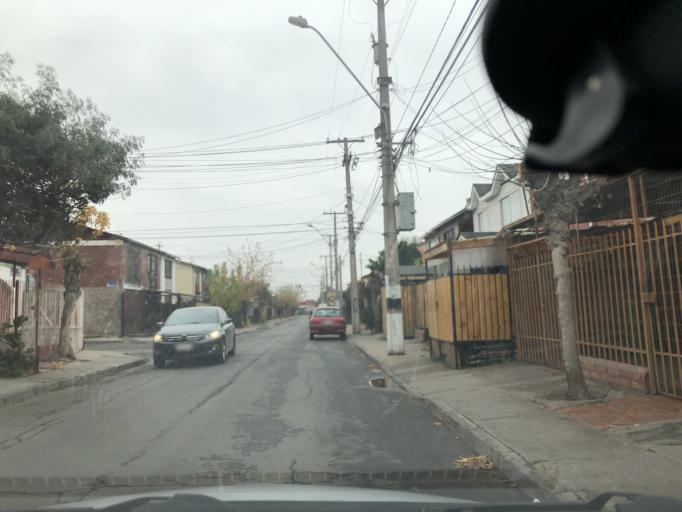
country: CL
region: Santiago Metropolitan
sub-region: Provincia de Cordillera
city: Puente Alto
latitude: -33.5847
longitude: -70.5930
